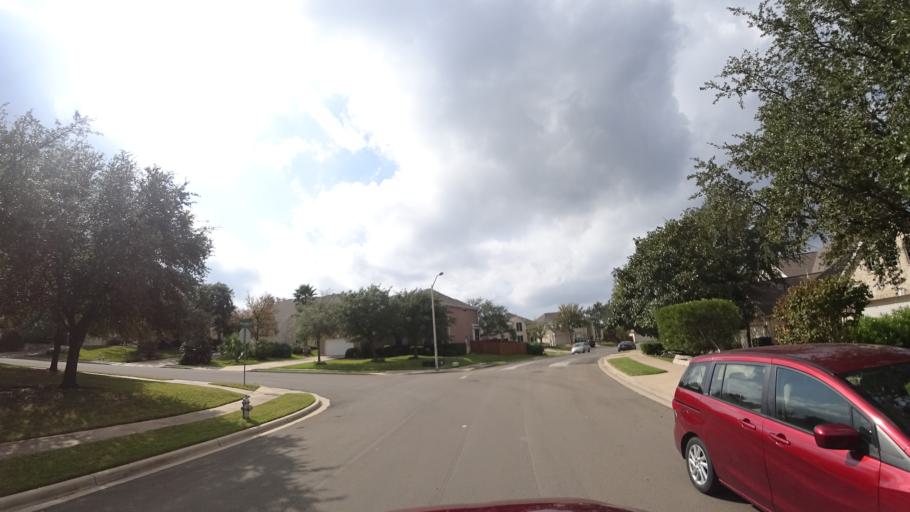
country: US
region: Texas
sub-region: Williamson County
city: Anderson Mill
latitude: 30.4232
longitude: -97.8634
